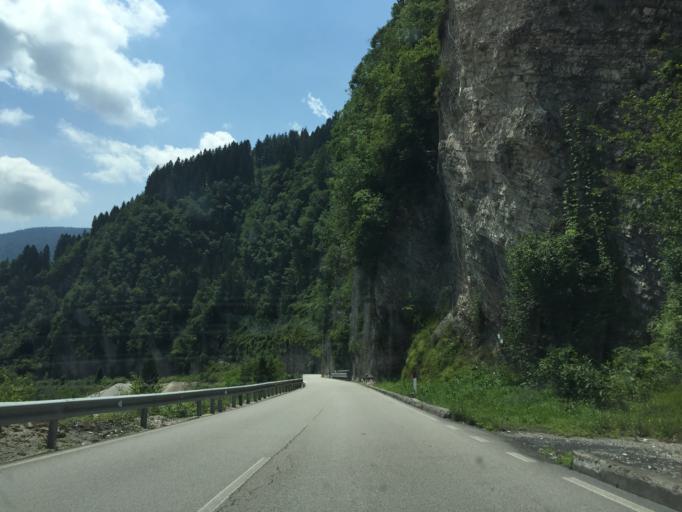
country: IT
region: Veneto
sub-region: Provincia di Belluno
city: Lamon
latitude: 46.0482
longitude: 11.7624
